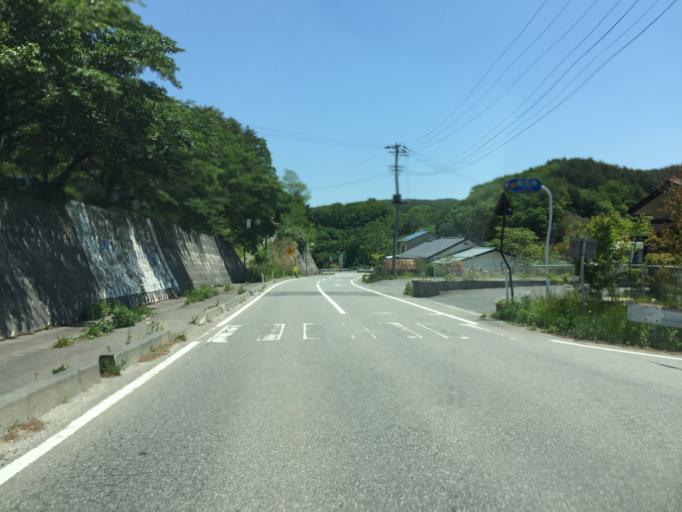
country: JP
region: Fukushima
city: Funehikimachi-funehiki
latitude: 37.5023
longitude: 140.7588
